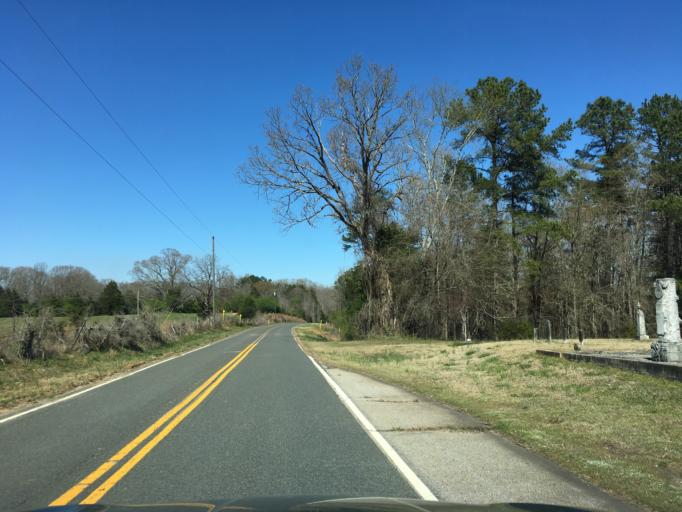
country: US
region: South Carolina
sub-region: Spartanburg County
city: Woodruff
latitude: 34.8159
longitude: -82.0828
